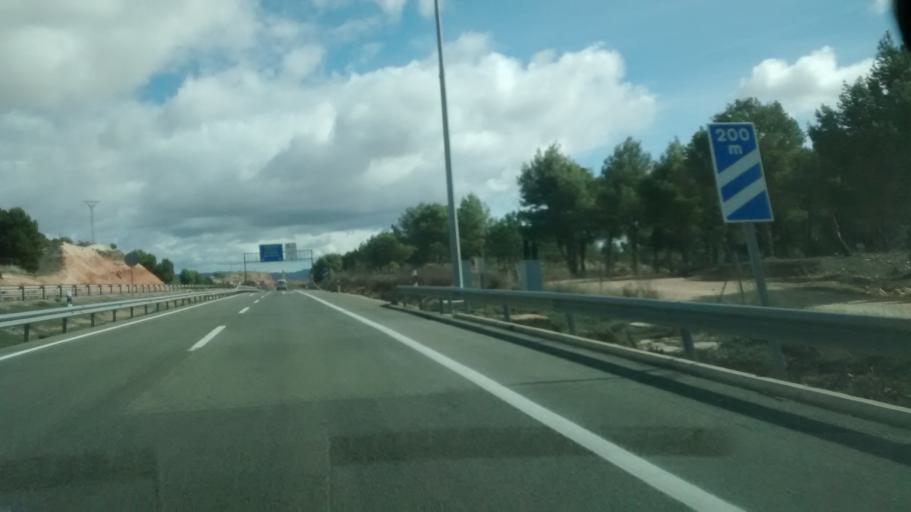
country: ES
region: Aragon
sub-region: Provincia de Zaragoza
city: Monreal de Ariza
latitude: 41.3100
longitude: -2.0850
